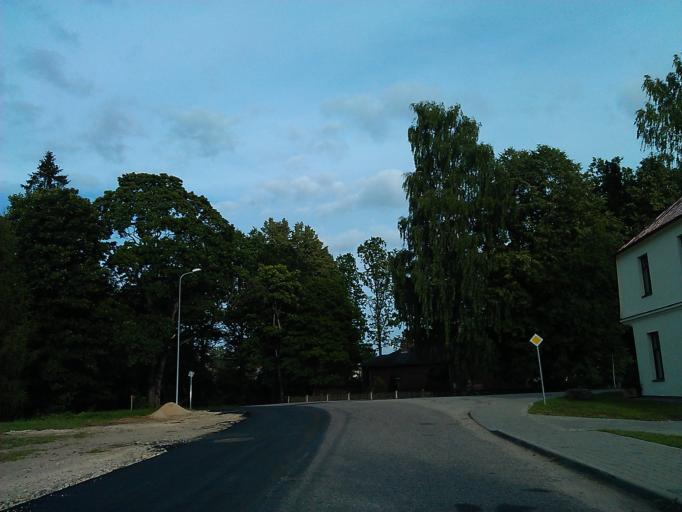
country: LV
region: Amatas Novads
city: Drabesi
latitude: 57.2013
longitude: 25.1723
